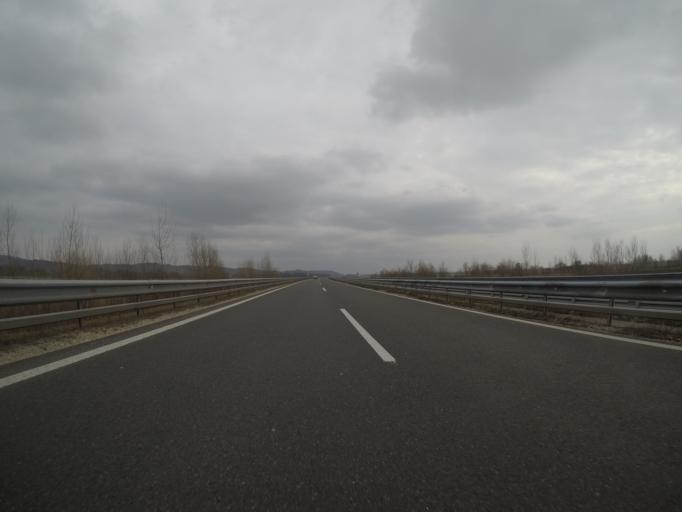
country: HR
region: Medimurska
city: Peklenica
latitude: 46.5329
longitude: 16.4765
